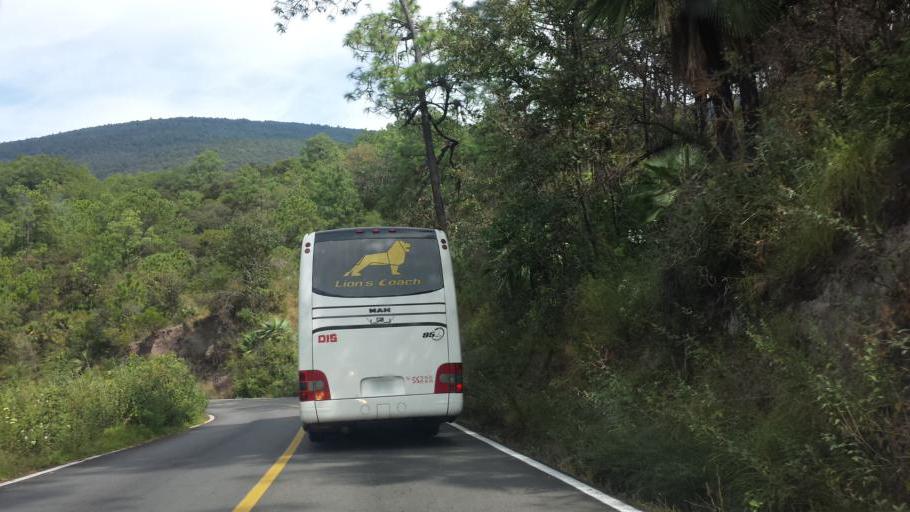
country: MX
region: Oaxaca
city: San Francisco Sola
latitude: 16.4521
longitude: -97.0316
